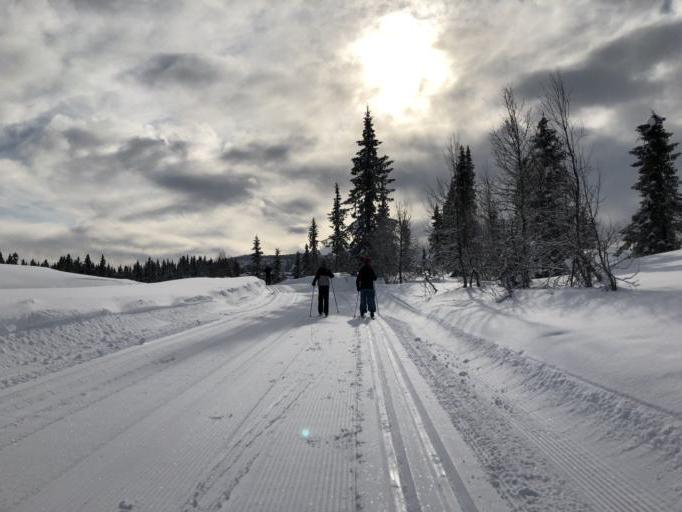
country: NO
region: Oppland
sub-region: Gausdal
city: Segalstad bru
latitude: 61.3161
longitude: 10.0642
